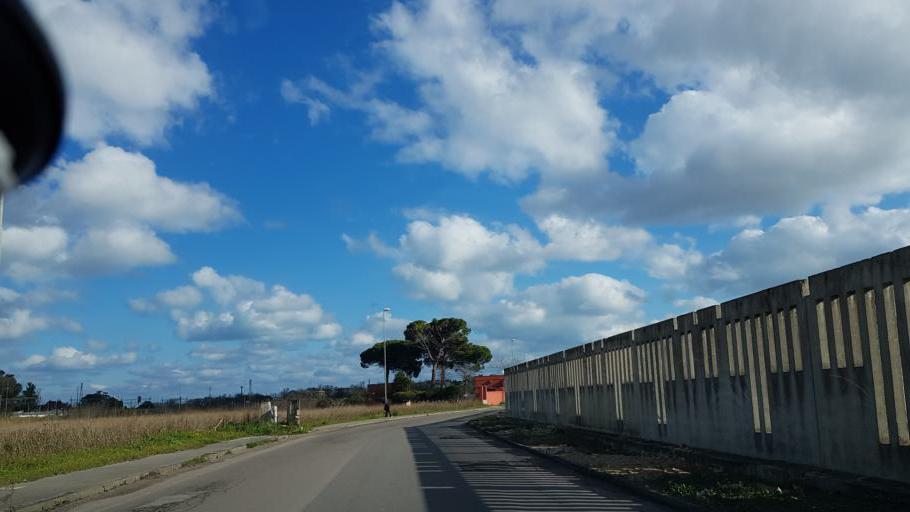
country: IT
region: Apulia
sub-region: Provincia di Brindisi
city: Brindisi
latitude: 40.6254
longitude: 17.9123
